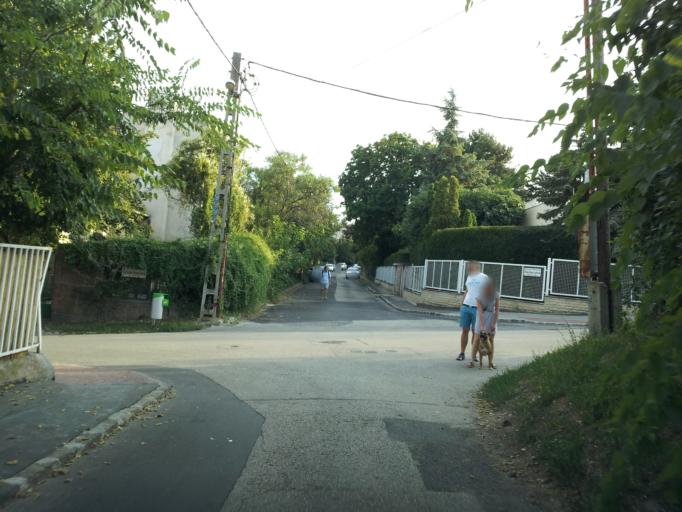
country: HU
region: Budapest
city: Budapest XII. keruelet
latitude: 47.4920
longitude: 19.0076
